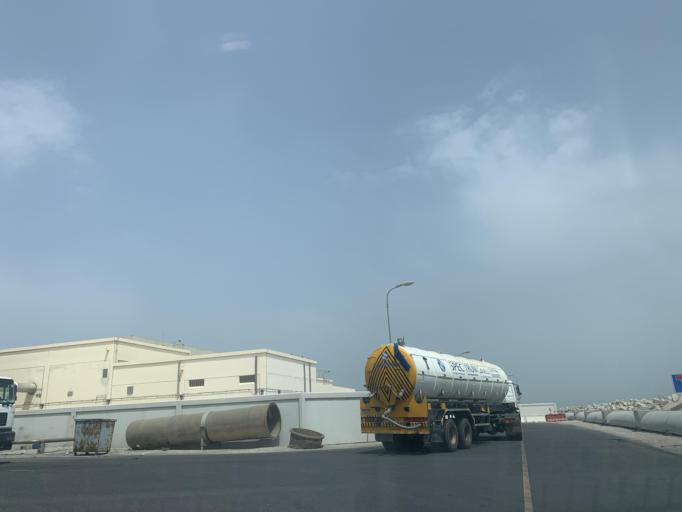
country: BH
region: Muharraq
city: Al Hadd
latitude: 26.2259
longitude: 50.7031
